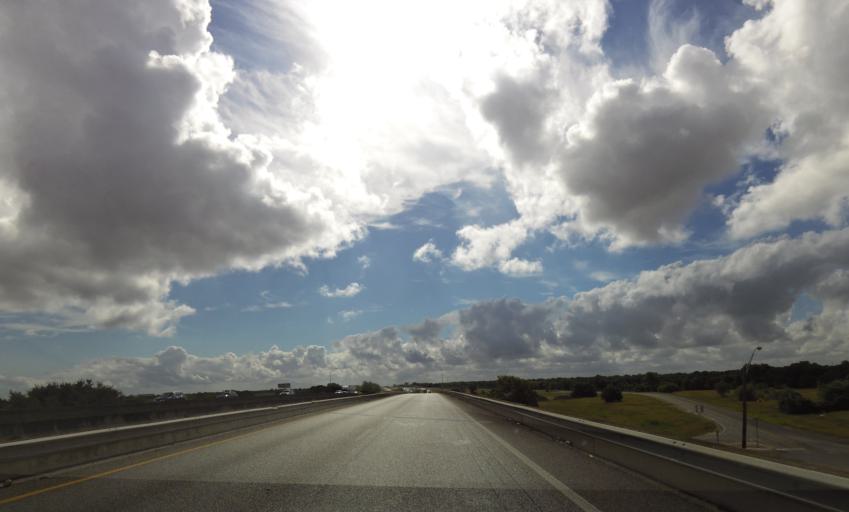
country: US
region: Texas
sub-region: Guadalupe County
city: Seguin
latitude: 29.5993
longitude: -97.9263
